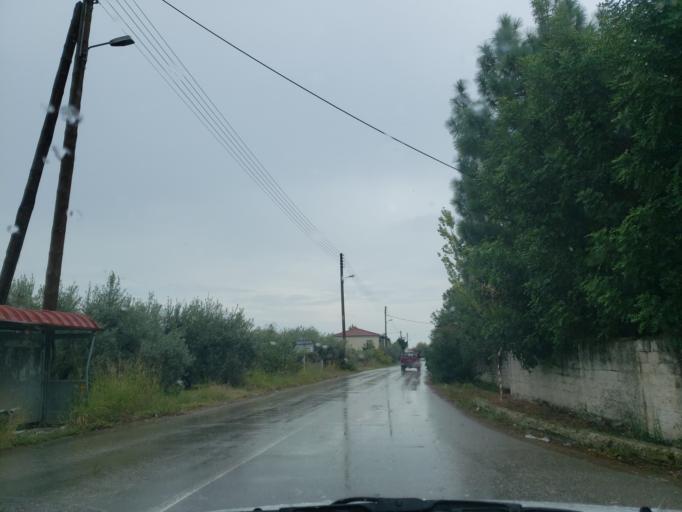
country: GR
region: Central Greece
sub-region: Nomos Fthiotidos
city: Anthili
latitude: 38.8044
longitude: 22.4430
